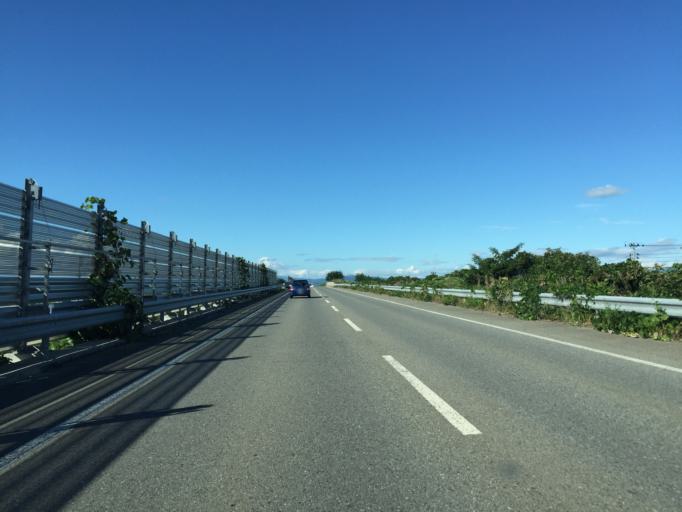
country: JP
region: Yamagata
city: Yonezawa
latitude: 37.9321
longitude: 140.1099
